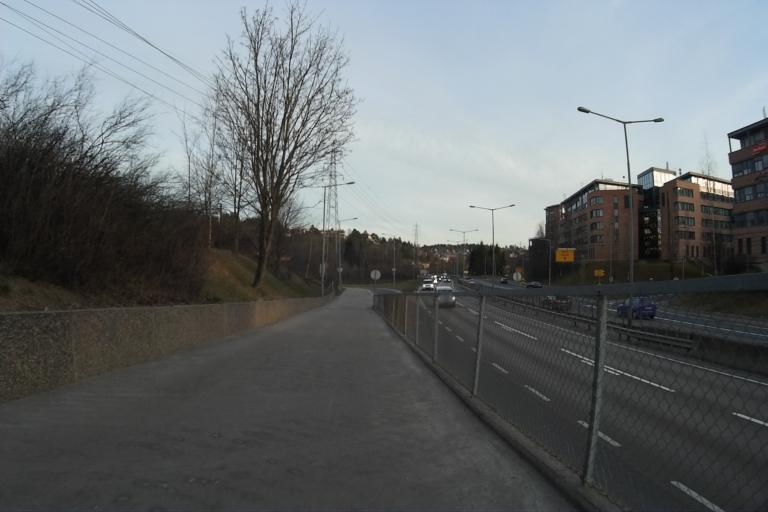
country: NO
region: Oslo
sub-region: Oslo
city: Oslo
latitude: 59.9120
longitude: 10.8174
